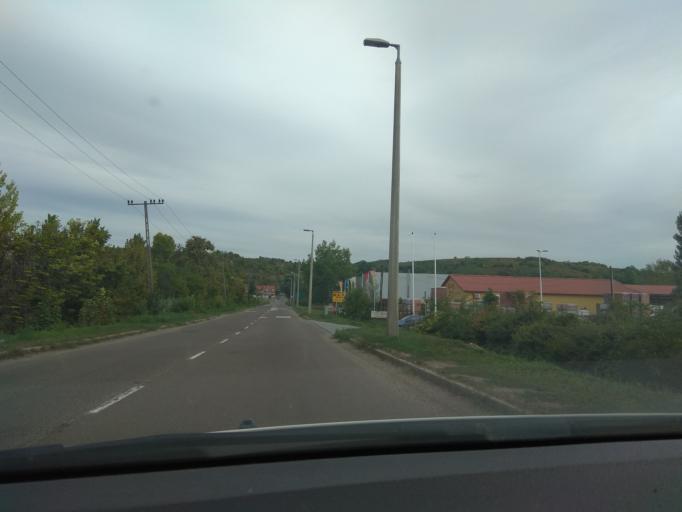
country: HU
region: Heves
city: Andornaktalya
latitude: 47.8719
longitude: 20.3977
